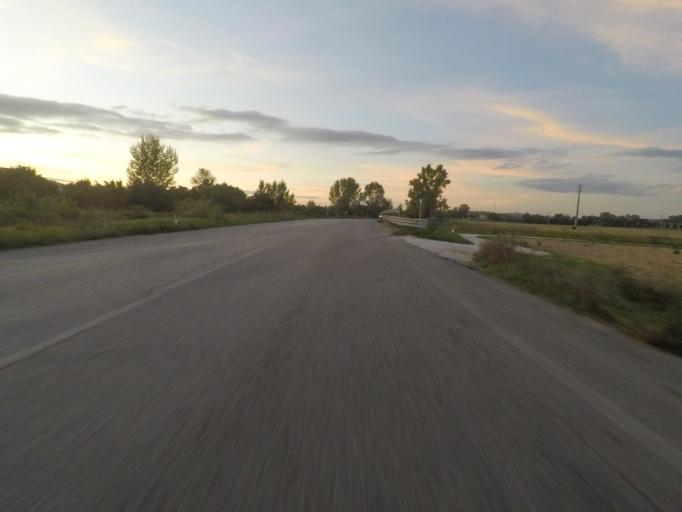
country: IT
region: Tuscany
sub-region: Provincia di Siena
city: Sinalunga
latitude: 43.2175
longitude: 11.7589
